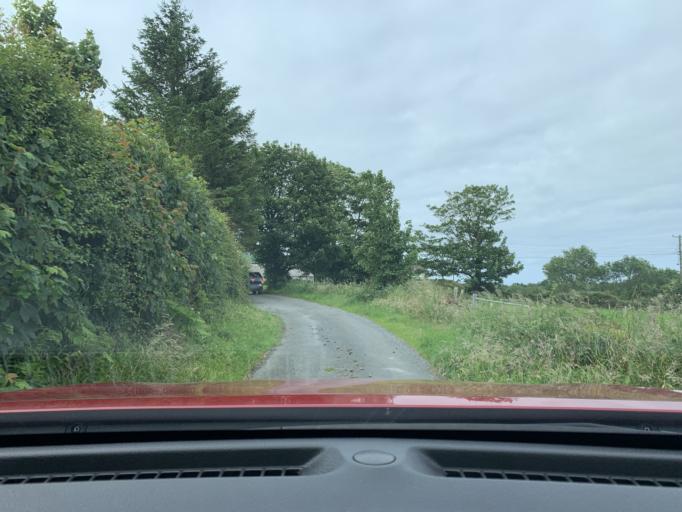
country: IE
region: Connaught
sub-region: Sligo
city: Sligo
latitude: 54.3767
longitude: -8.5206
